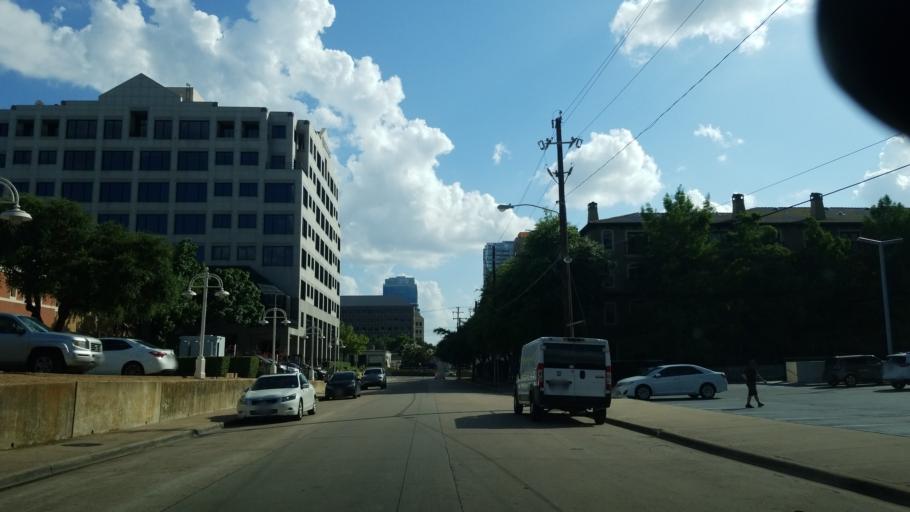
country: US
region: Texas
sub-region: Dallas County
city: Dallas
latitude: 32.7997
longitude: -96.8035
